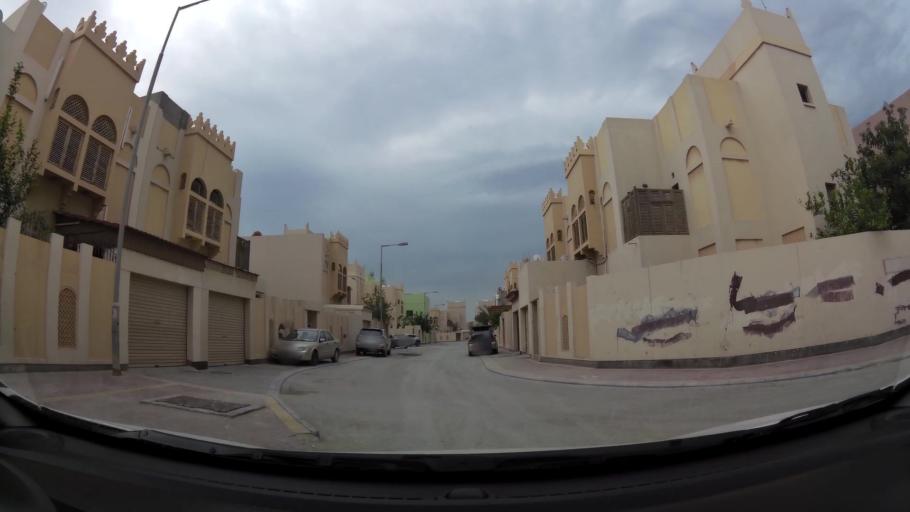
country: BH
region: Manama
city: Manama
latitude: 26.1835
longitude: 50.5828
